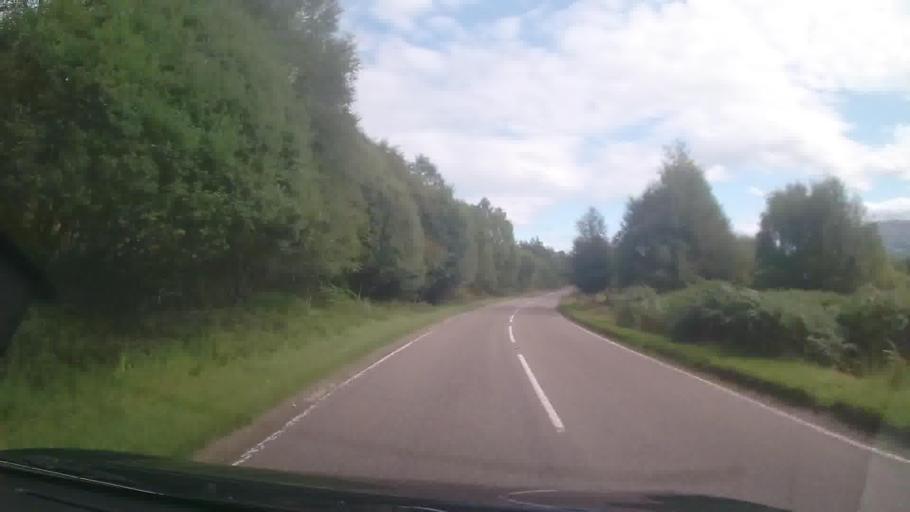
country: GB
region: Scotland
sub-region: Highland
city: Fort William
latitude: 56.6966
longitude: -5.3296
